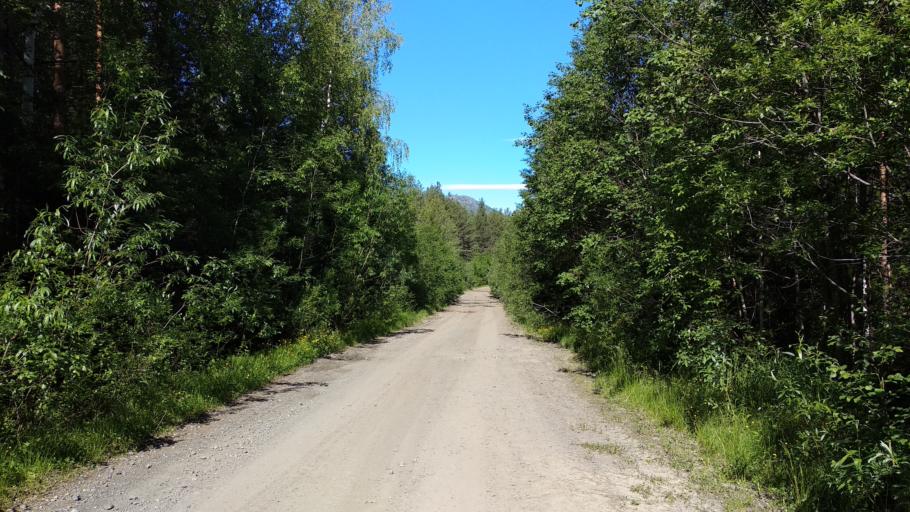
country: RU
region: Sverdlovsk
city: Severoural'sk
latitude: 60.1249
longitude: 59.7413
